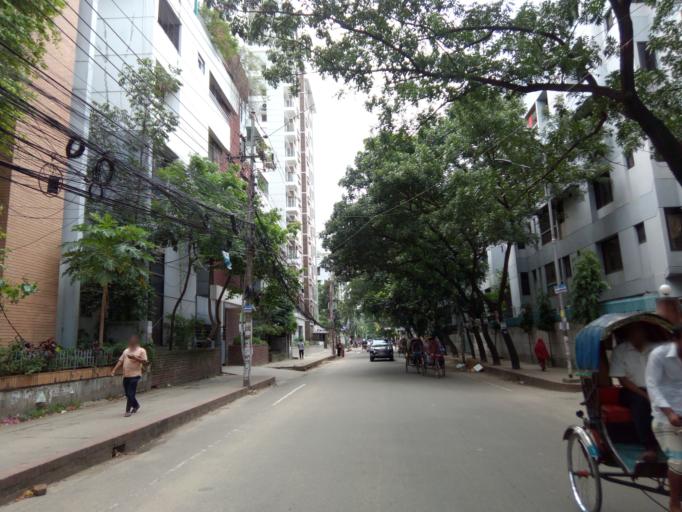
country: BD
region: Dhaka
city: Azimpur
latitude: 23.7463
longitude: 90.3741
